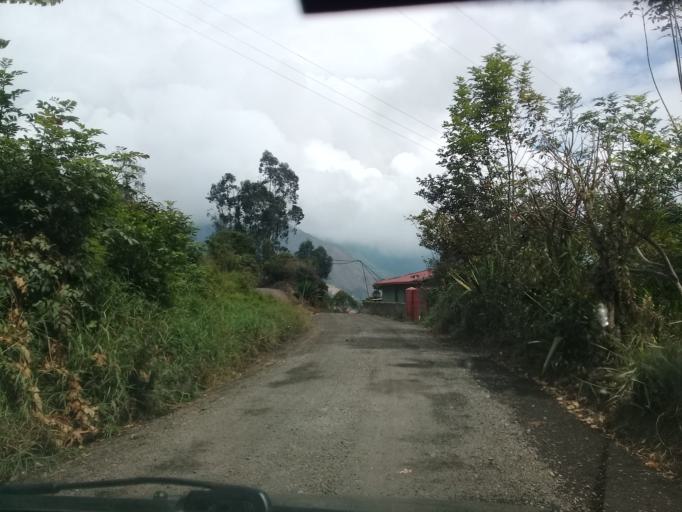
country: CO
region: Cundinamarca
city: Une
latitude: 4.4074
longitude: -73.9914
